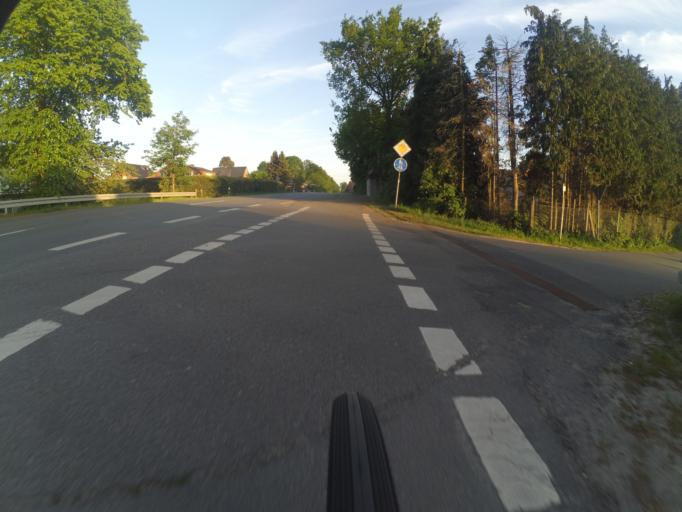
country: DE
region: North Rhine-Westphalia
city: Ibbenburen
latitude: 52.3274
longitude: 7.6677
